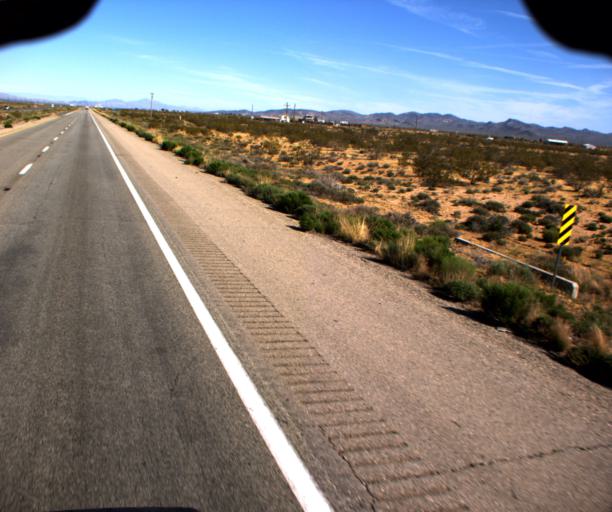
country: US
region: Arizona
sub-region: Mohave County
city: Dolan Springs
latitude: 35.5150
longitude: -114.3421
